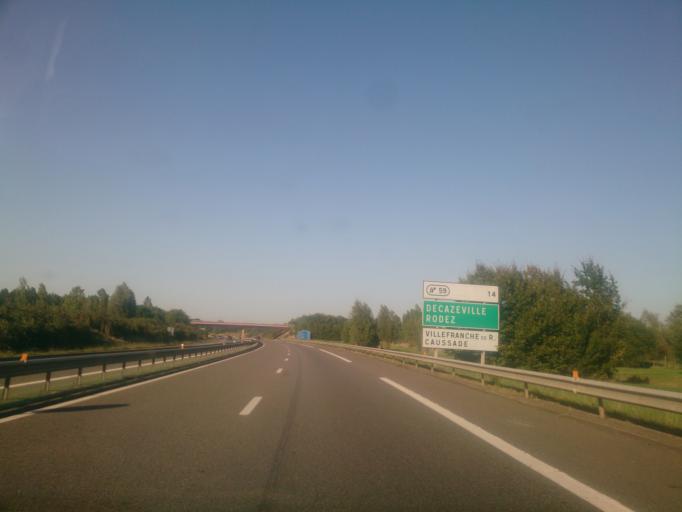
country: FR
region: Midi-Pyrenees
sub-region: Departement du Tarn-et-Garonne
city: Albias
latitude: 44.0562
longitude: 1.4185
